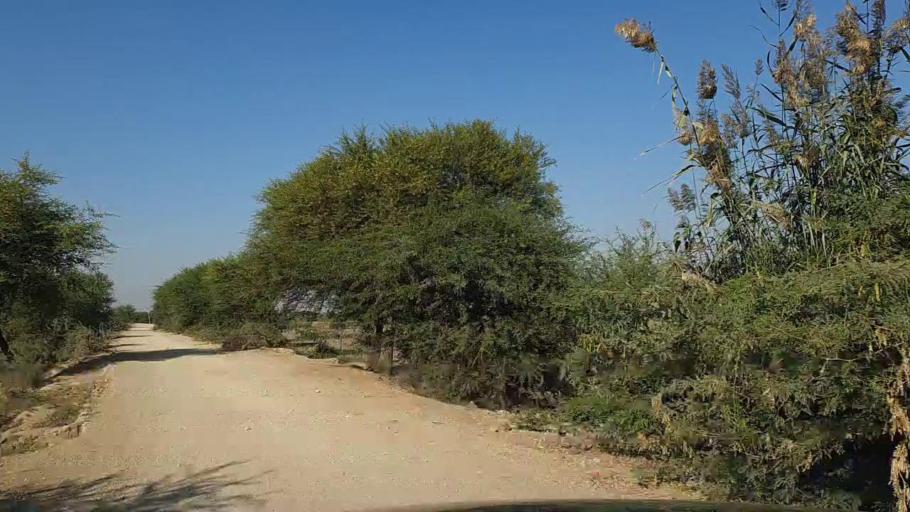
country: PK
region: Sindh
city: Mirpur Batoro
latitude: 24.7315
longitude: 68.3456
